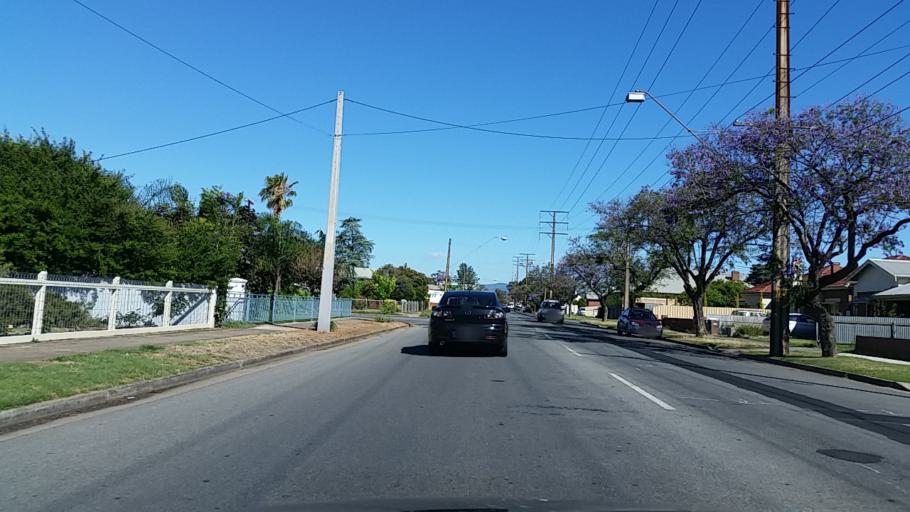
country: AU
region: South Australia
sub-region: Port Adelaide Enfield
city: Alberton
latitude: -34.8618
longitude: 138.5264
